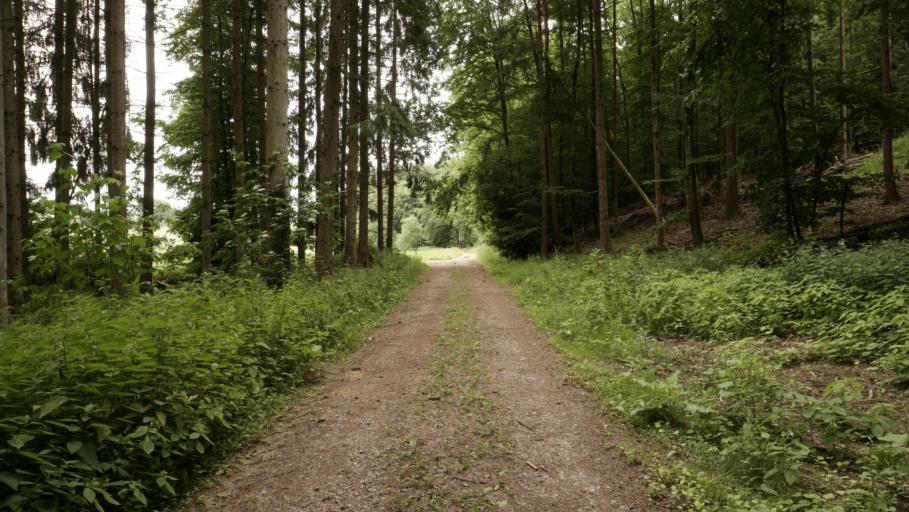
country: DE
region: Baden-Wuerttemberg
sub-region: Karlsruhe Region
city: Mosbach
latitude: 49.3383
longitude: 9.2014
